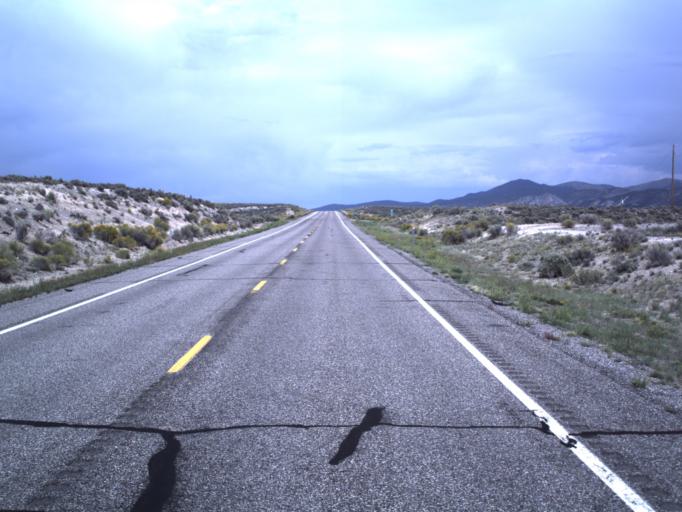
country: US
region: Utah
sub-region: Garfield County
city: Panguitch
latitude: 37.9755
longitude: -112.4052
